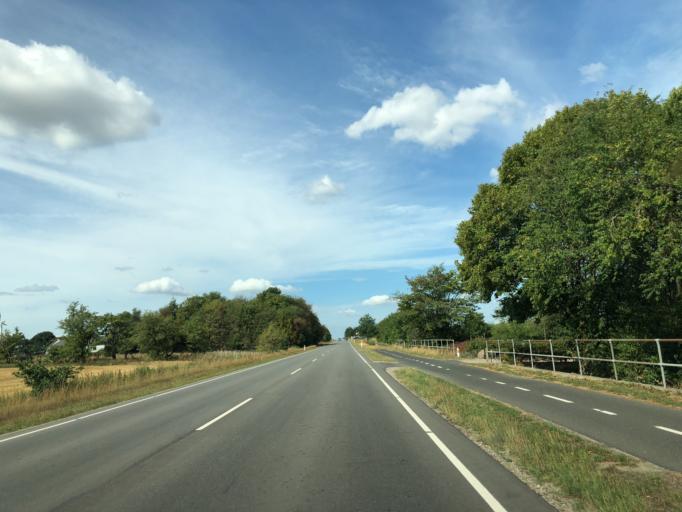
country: DK
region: Central Jutland
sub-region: Ikast-Brande Kommune
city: Bording Kirkeby
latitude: 56.1419
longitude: 9.2547
